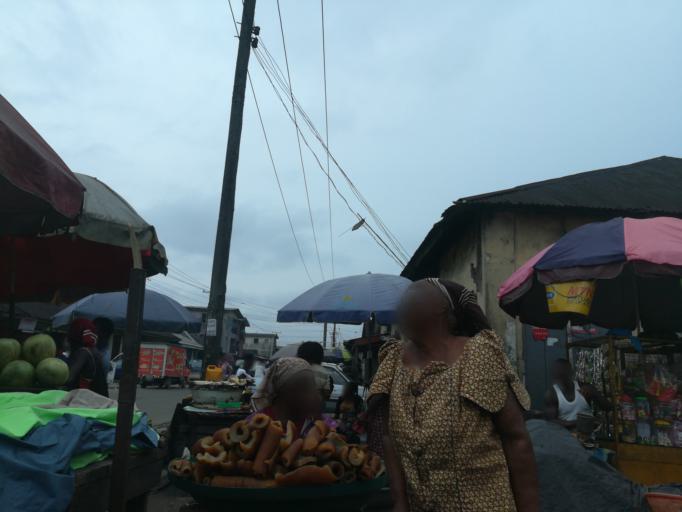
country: NG
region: Rivers
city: Port Harcourt
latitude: 4.7594
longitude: 7.0259
